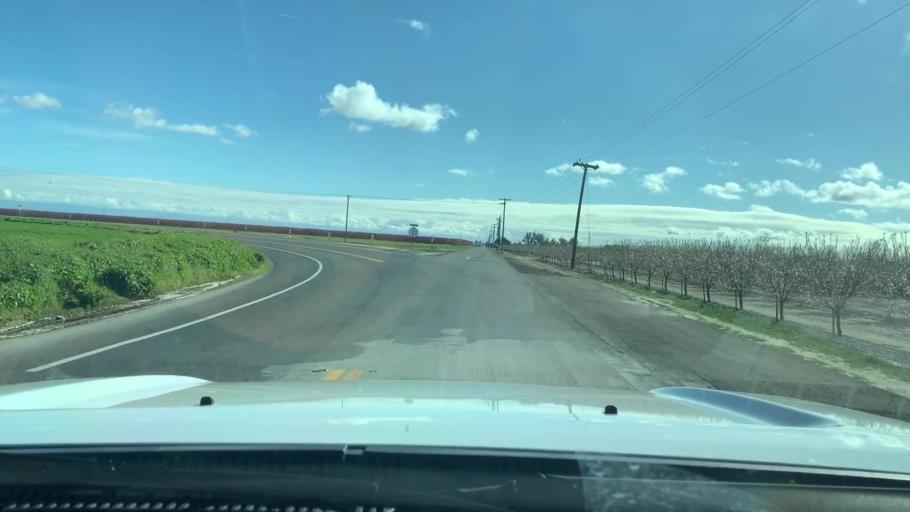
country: US
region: California
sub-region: Fresno County
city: Laton
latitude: 36.4893
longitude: -119.6847
